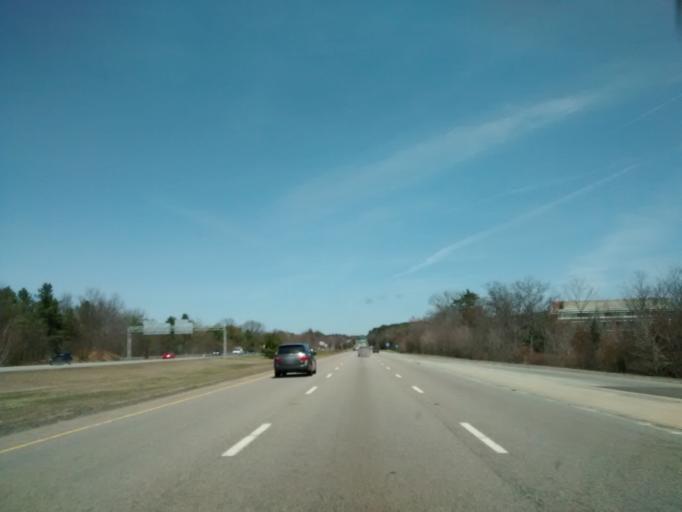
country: US
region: Massachusetts
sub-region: Worcester County
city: Northborough
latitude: 42.3480
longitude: -71.6214
